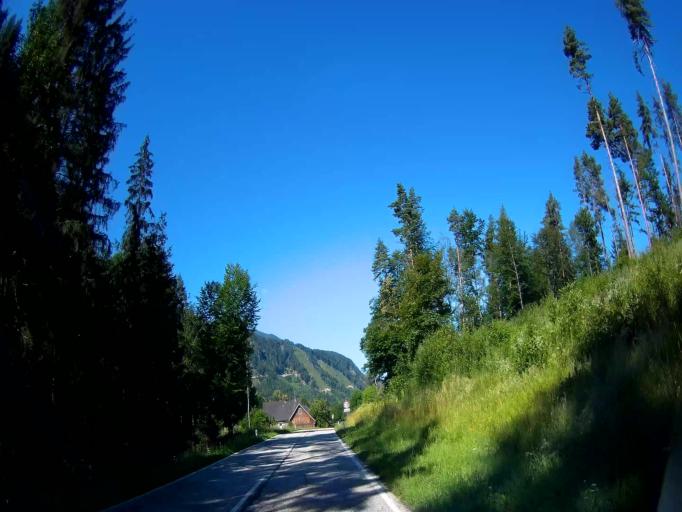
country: AT
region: Carinthia
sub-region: Politischer Bezirk Klagenfurt Land
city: Grafenstein
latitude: 46.5404
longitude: 14.4115
